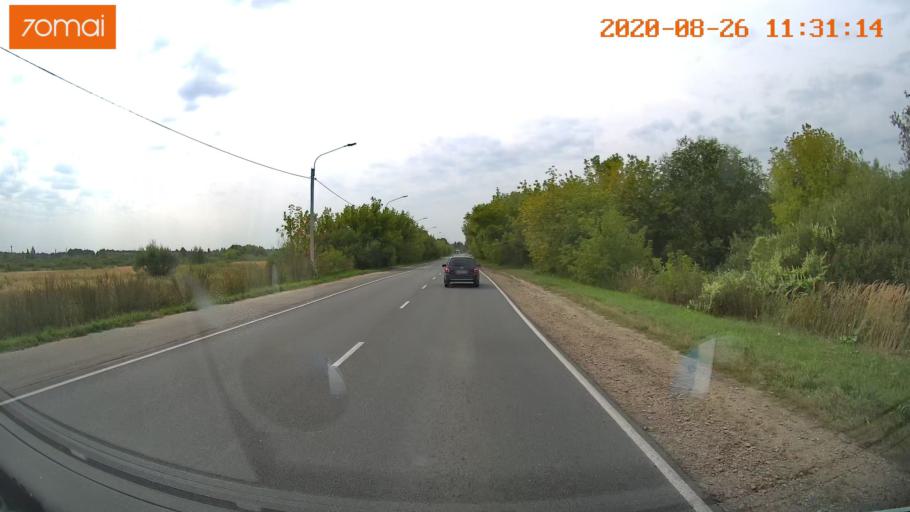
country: RU
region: Rjazan
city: Shilovo
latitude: 54.3083
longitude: 40.8754
